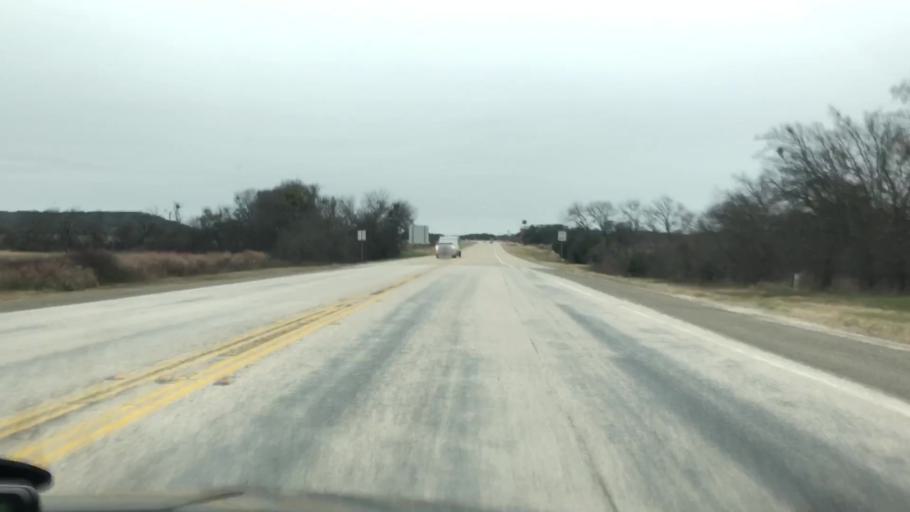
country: US
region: Texas
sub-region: Hamilton County
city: Hamilton
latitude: 31.4848
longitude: -98.1494
